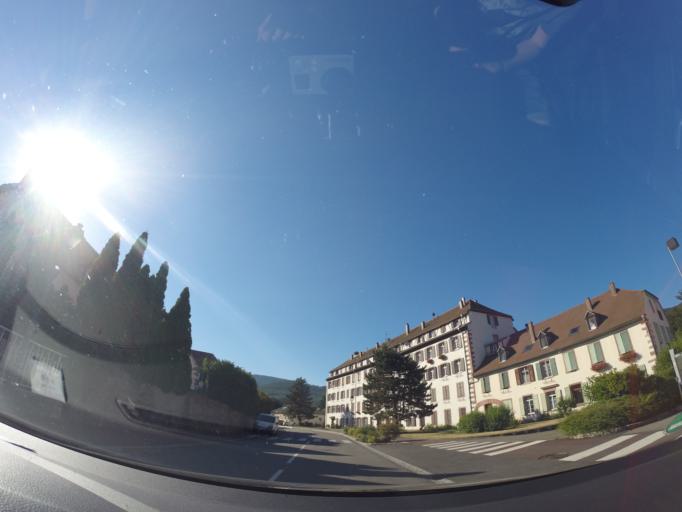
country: FR
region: Alsace
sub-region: Departement du Haut-Rhin
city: Kaysersberg
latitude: 48.1446
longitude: 7.2558
